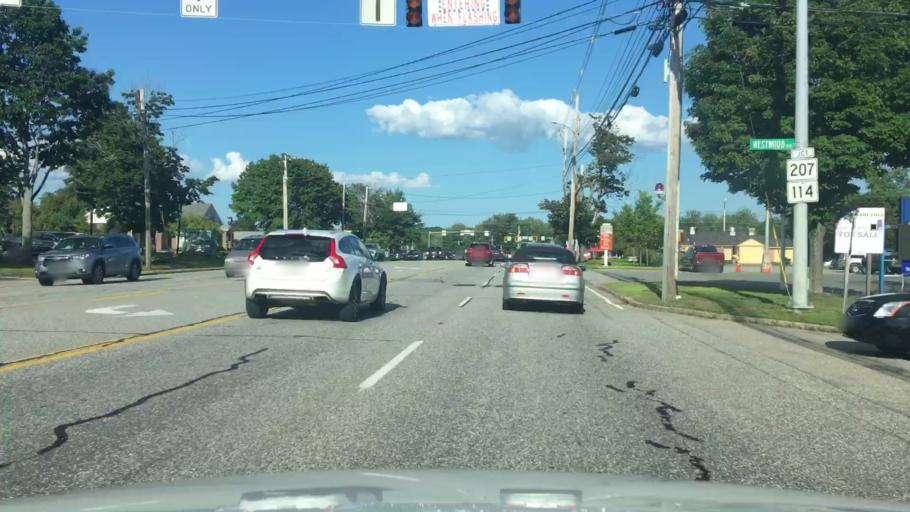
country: US
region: Maine
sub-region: Cumberland County
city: Scarborough
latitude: 43.5897
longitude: -70.3368
